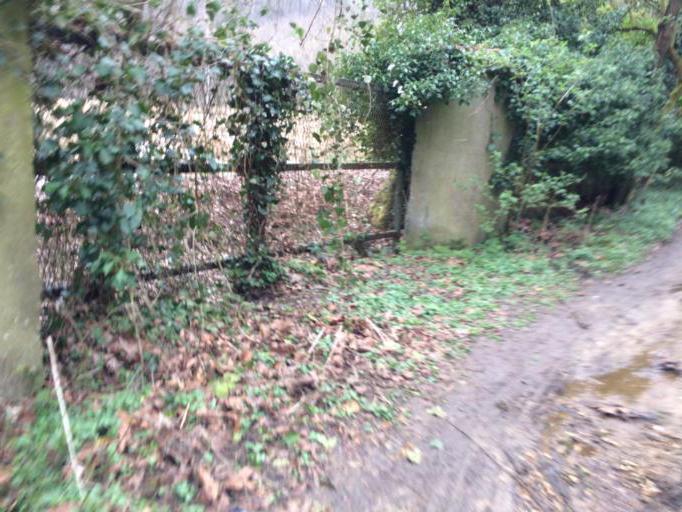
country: FR
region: Ile-de-France
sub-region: Departement des Yvelines
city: Les Loges-en-Josas
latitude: 48.7573
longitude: 2.1527
